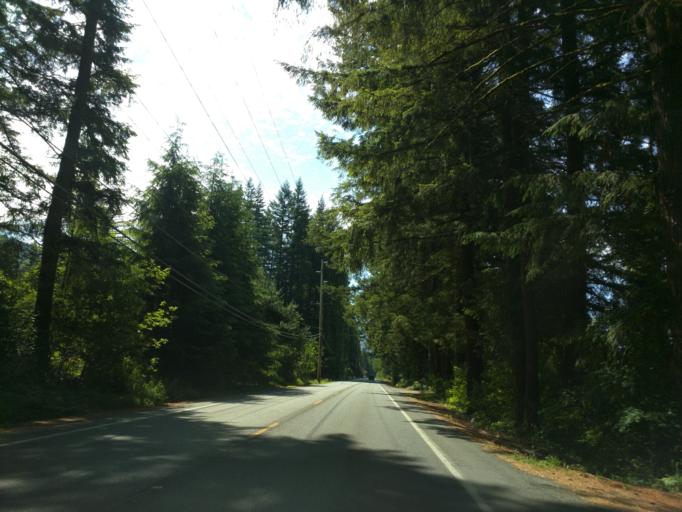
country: US
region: Washington
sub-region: Whatcom County
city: Peaceful Valley
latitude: 48.9428
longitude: -122.1499
